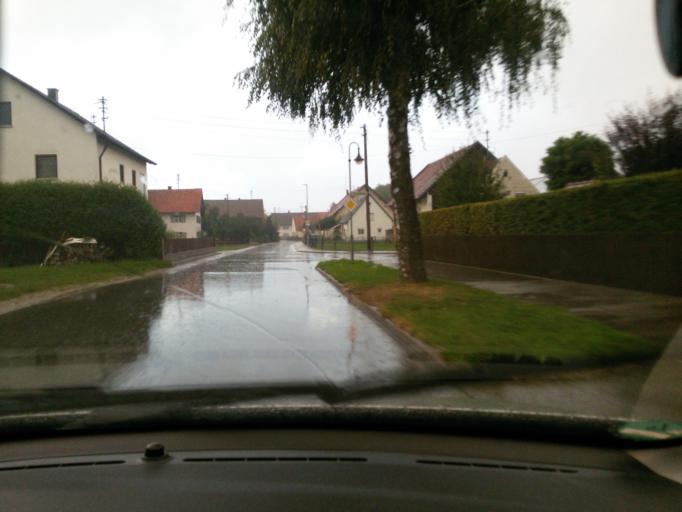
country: DE
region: Bavaria
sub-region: Swabia
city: Hiltenfingen
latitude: 48.1592
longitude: 10.7194
